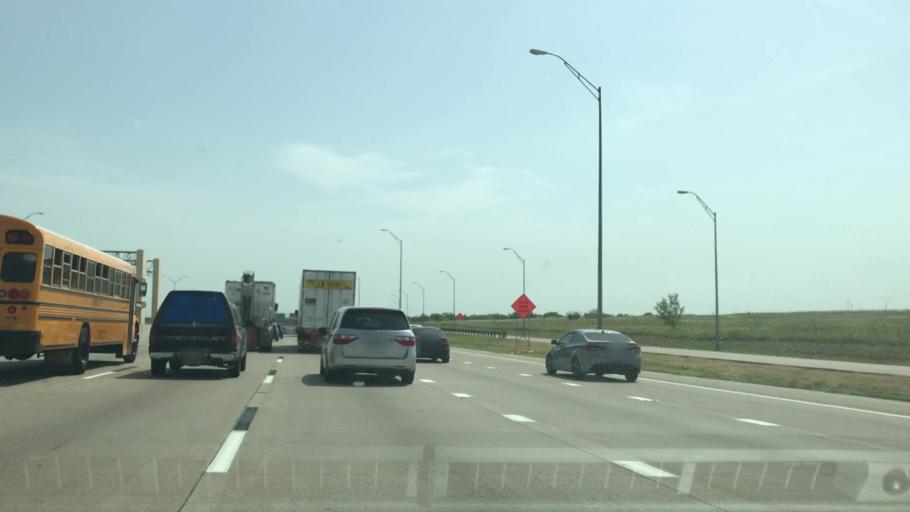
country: US
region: Texas
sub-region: Tarrant County
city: Grapevine
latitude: 32.9257
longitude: -97.0553
